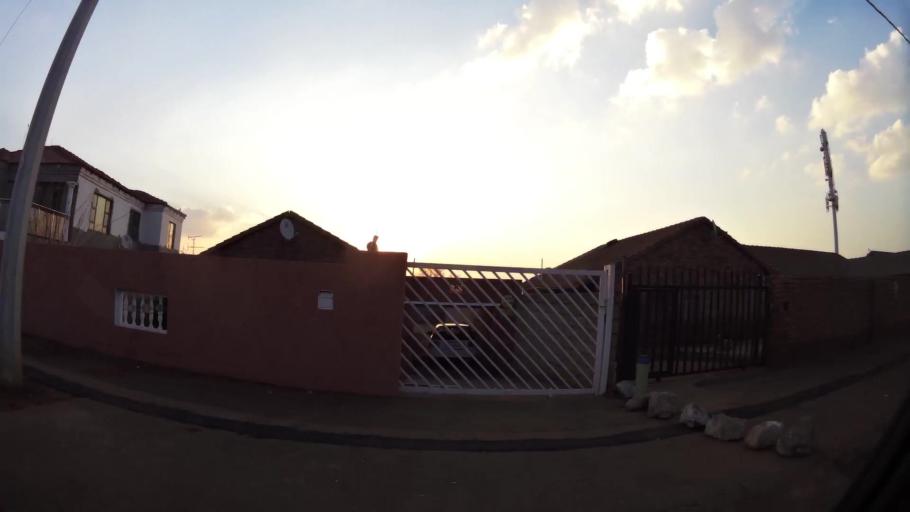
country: ZA
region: Gauteng
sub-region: City of Johannesburg Metropolitan Municipality
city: Soweto
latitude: -26.2892
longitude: 27.8891
